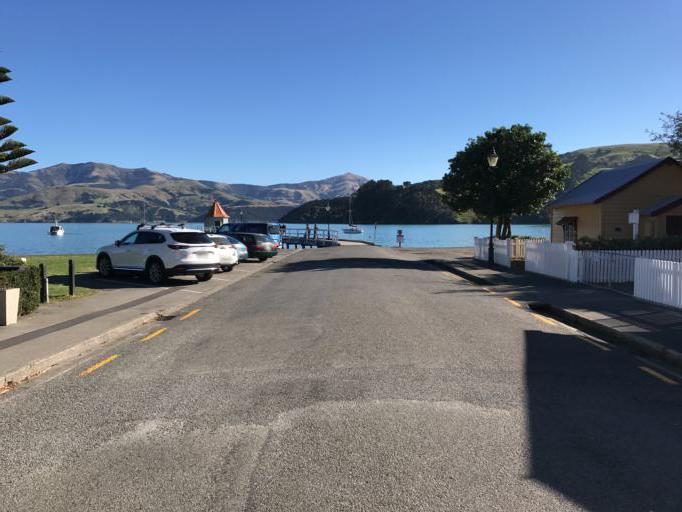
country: NZ
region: Canterbury
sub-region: Christchurch City
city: Christchurch
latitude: -43.8048
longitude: 172.9659
